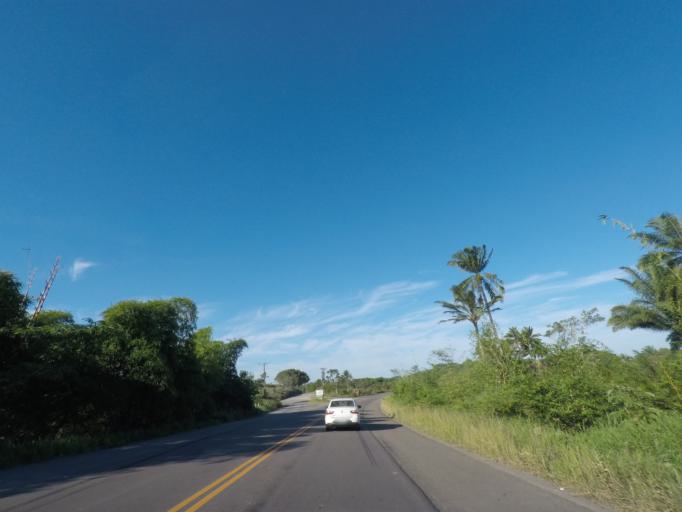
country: BR
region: Bahia
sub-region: Nazare
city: Nazare
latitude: -13.0191
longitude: -38.9861
